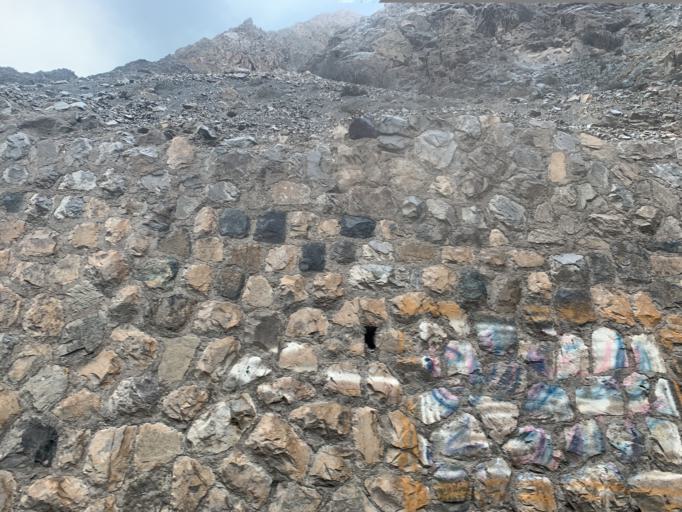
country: IR
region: Mazandaran
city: Amol
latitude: 36.1100
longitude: 52.2798
